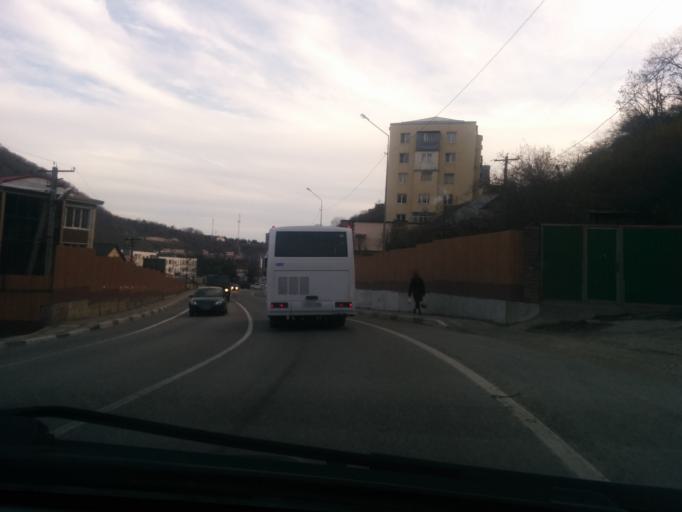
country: RU
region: Krasnodarskiy
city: Ol'ginka
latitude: 44.2027
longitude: 38.8864
